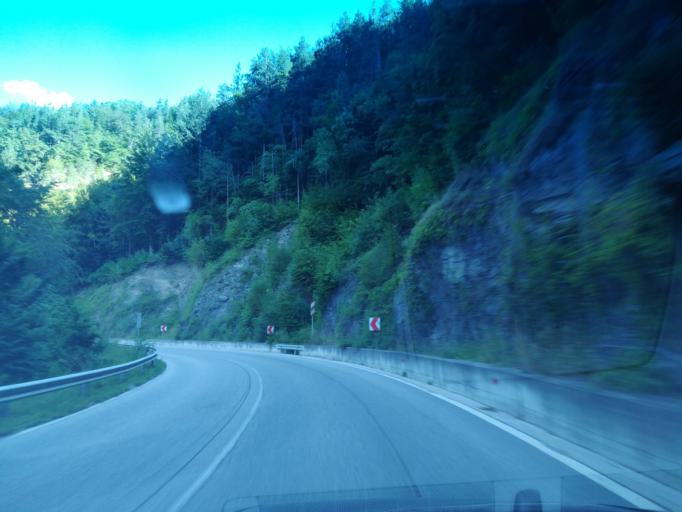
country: BG
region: Smolyan
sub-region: Obshtina Chepelare
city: Chepelare
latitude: 41.8222
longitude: 24.6922
